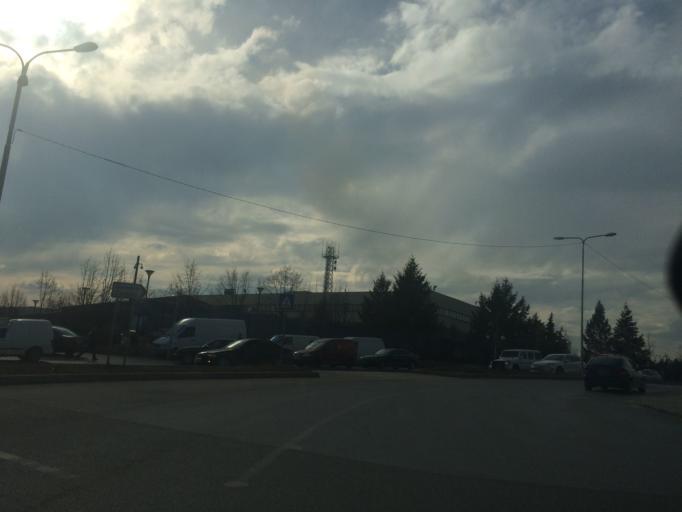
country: XK
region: Pristina
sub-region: Komuna e Prishtines
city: Pristina
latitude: 42.6456
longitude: 21.1693
